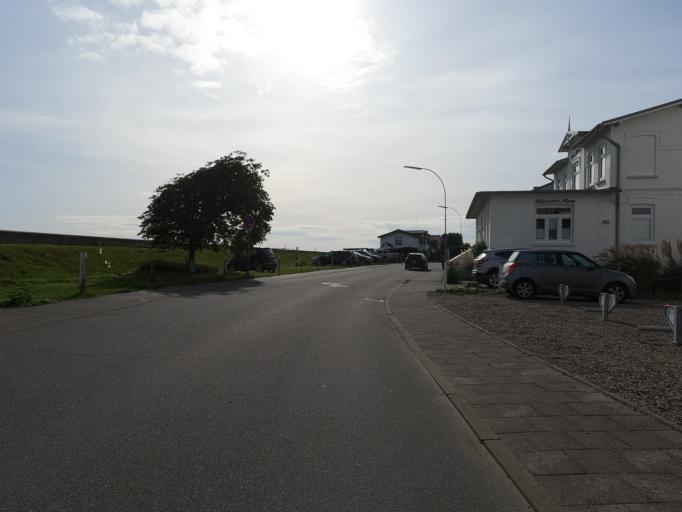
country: DE
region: Schleswig-Holstein
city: Dahme
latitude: 54.2188
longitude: 11.0895
